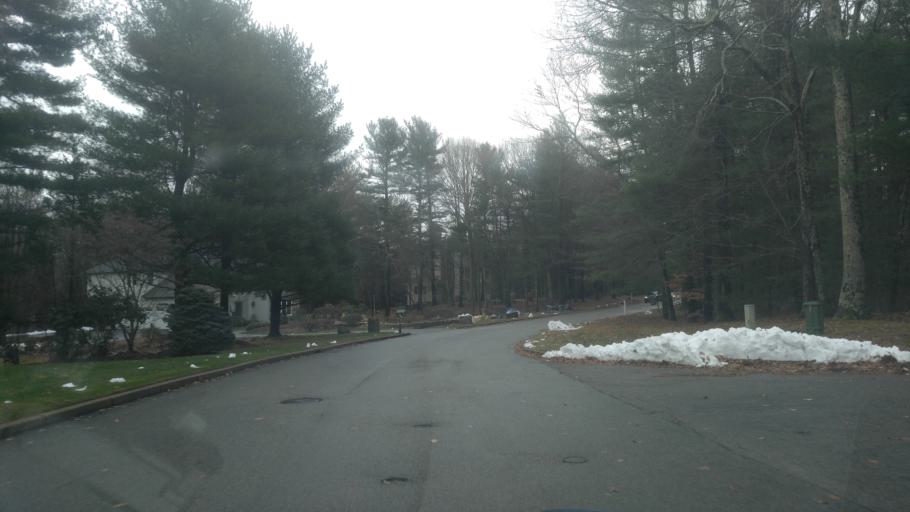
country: US
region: Rhode Island
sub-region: Kent County
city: West Warwick
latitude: 41.6505
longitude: -71.5343
